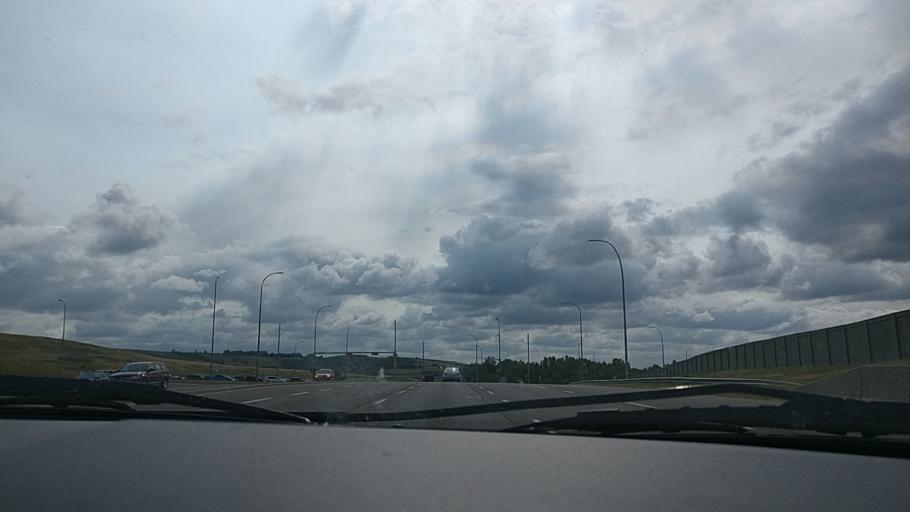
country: CA
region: Alberta
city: Calgary
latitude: 51.1099
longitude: -114.1421
